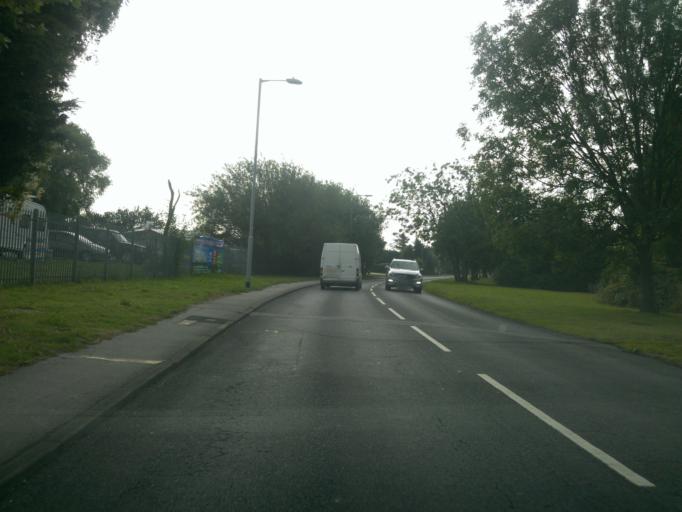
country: GB
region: England
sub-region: Essex
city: Little Clacton
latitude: 51.8150
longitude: 1.1483
